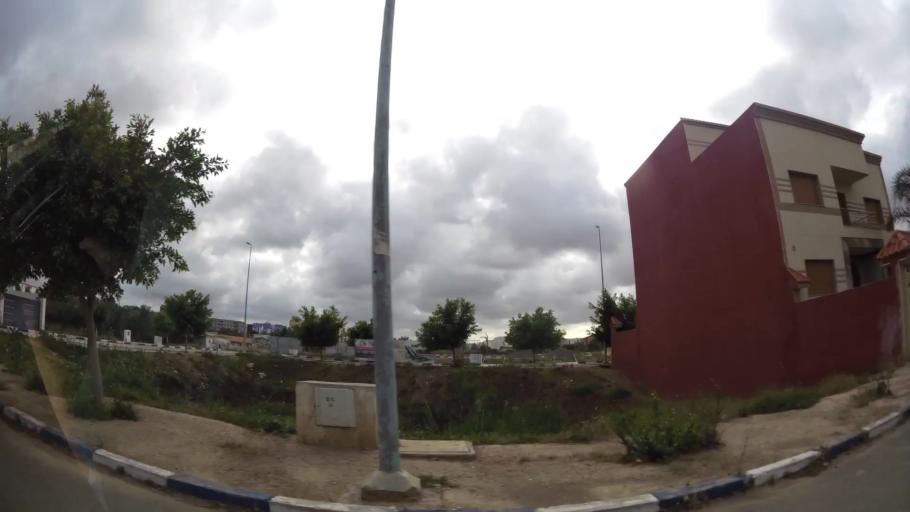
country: MA
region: Oriental
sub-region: Nador
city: Nador
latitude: 35.1581
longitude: -2.9184
